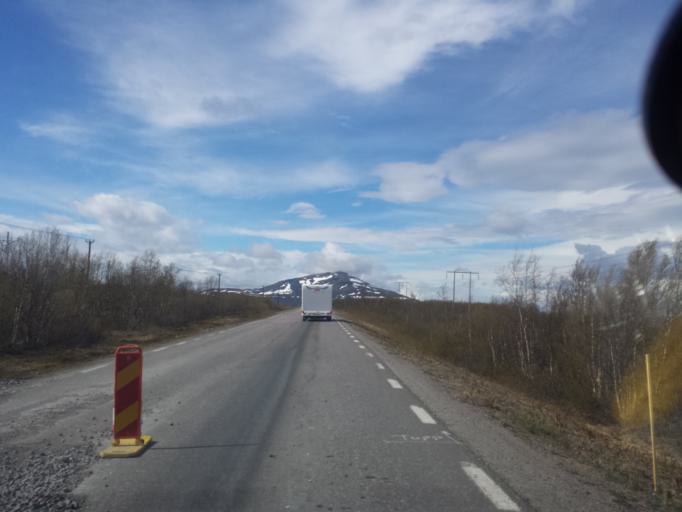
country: SE
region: Norrbotten
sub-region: Kiruna Kommun
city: Kiruna
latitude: 68.1135
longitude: 19.8315
